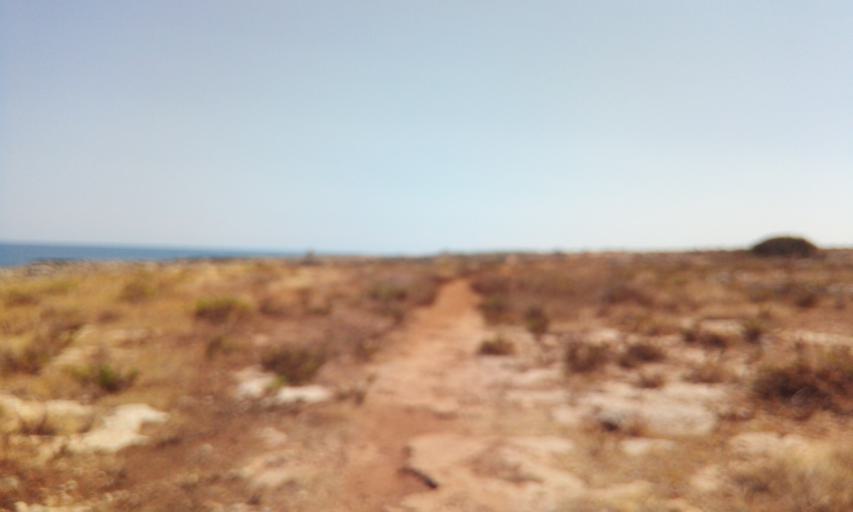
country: IT
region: Apulia
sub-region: Provincia di Bari
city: Polignano a Mare
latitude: 40.9858
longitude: 17.2457
